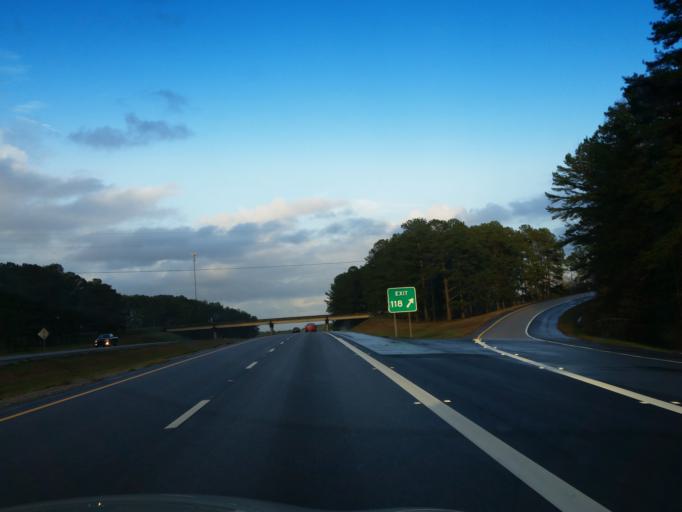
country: US
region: Mississippi
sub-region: Jones County
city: Sharon
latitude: 31.9628
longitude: -88.9693
